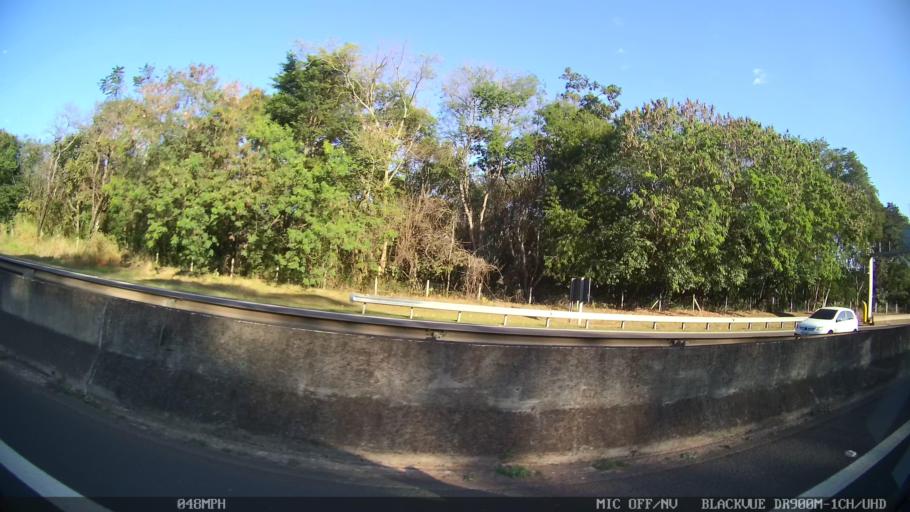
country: BR
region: Sao Paulo
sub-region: Piracicaba
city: Piracicaba
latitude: -22.7017
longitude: -47.6437
